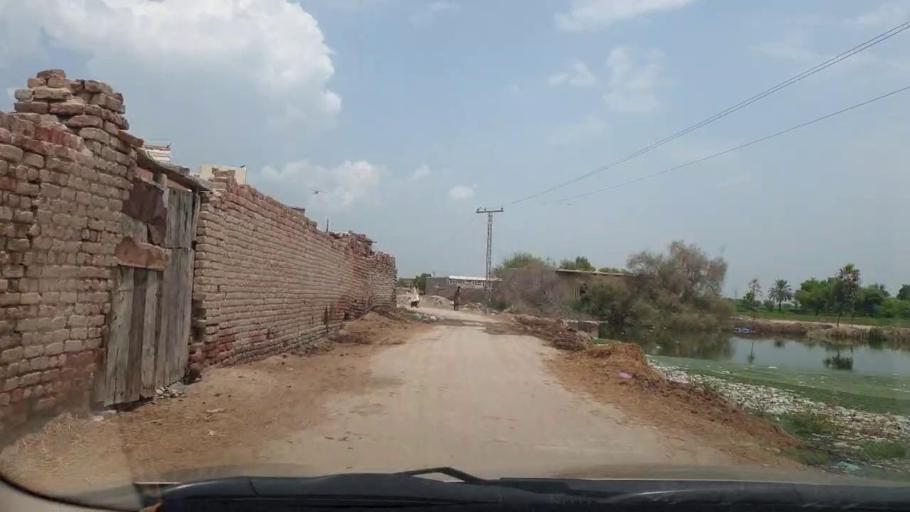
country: PK
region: Sindh
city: Larkana
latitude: 27.5660
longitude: 68.1261
